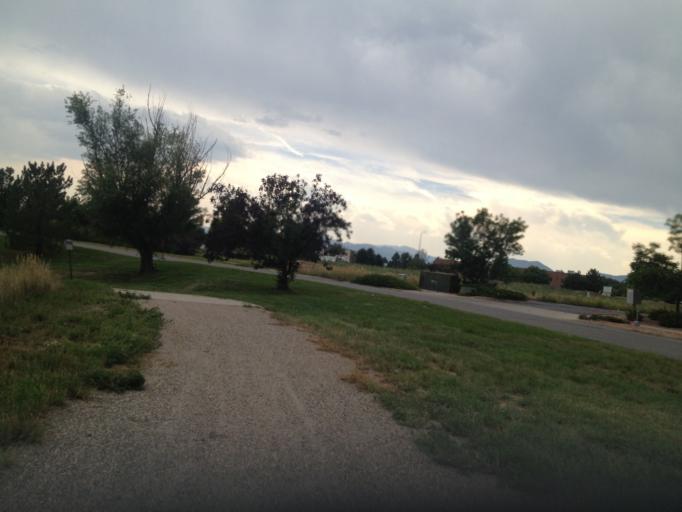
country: US
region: Colorado
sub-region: Boulder County
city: Lafayette
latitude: 39.9808
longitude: -105.0700
